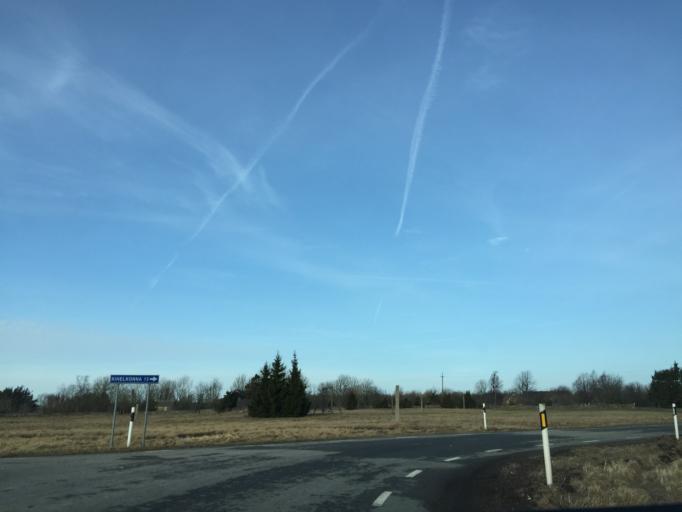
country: EE
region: Saare
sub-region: Kuressaare linn
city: Kuressaare
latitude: 58.2666
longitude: 21.9108
